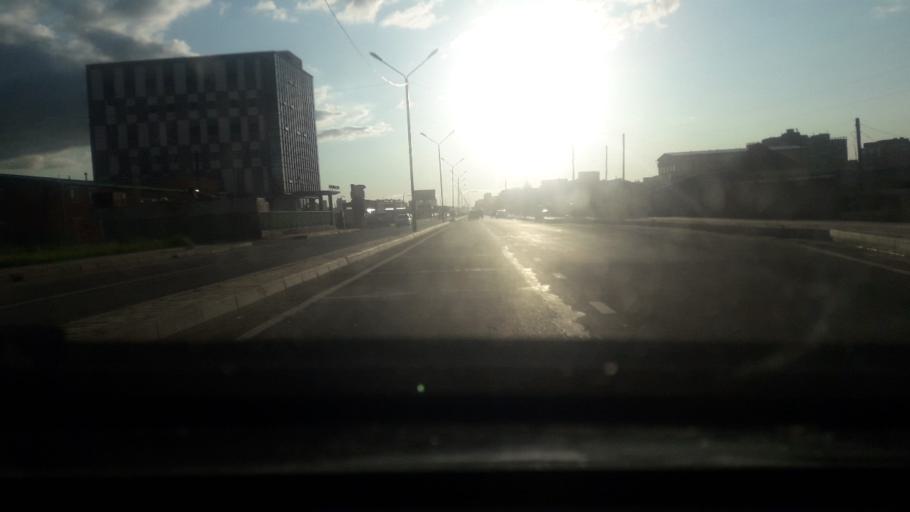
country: MN
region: Ulaanbaatar
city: Ulaanbaatar
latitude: 47.9081
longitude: 106.9670
